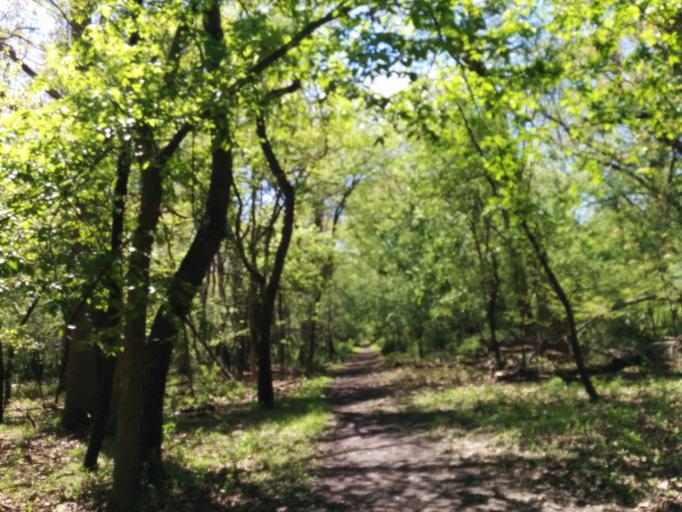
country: US
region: Illinois
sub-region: Cook County
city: Schiller Park
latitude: 41.9719
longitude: -87.8513
